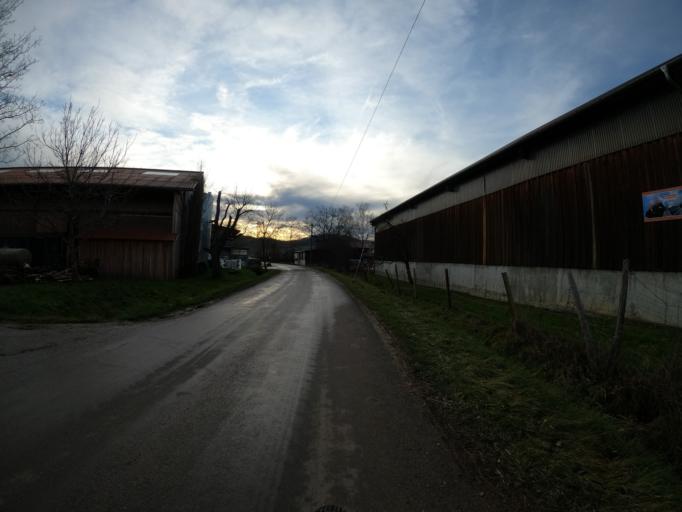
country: DE
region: Baden-Wuerttemberg
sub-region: Regierungsbezirk Stuttgart
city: Boll
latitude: 48.6462
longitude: 9.6004
